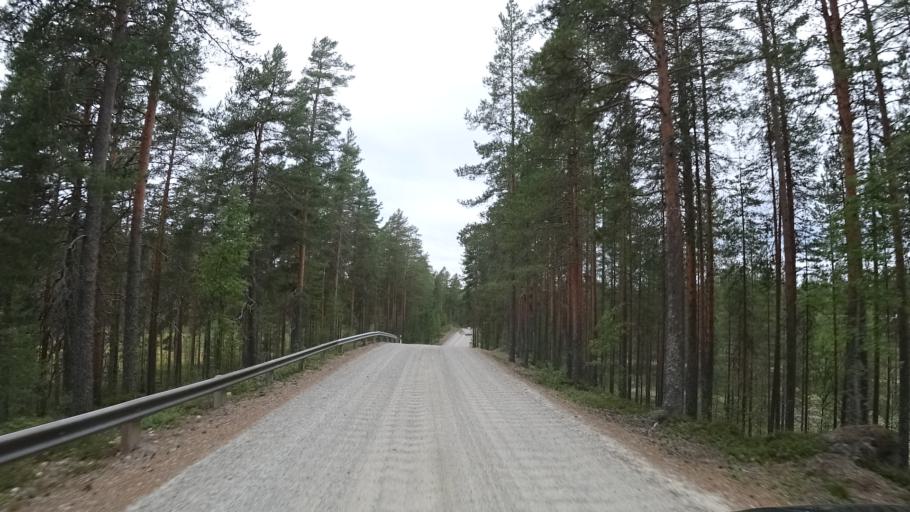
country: FI
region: North Karelia
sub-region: Pielisen Karjala
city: Lieksa
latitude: 63.2373
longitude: 30.3586
